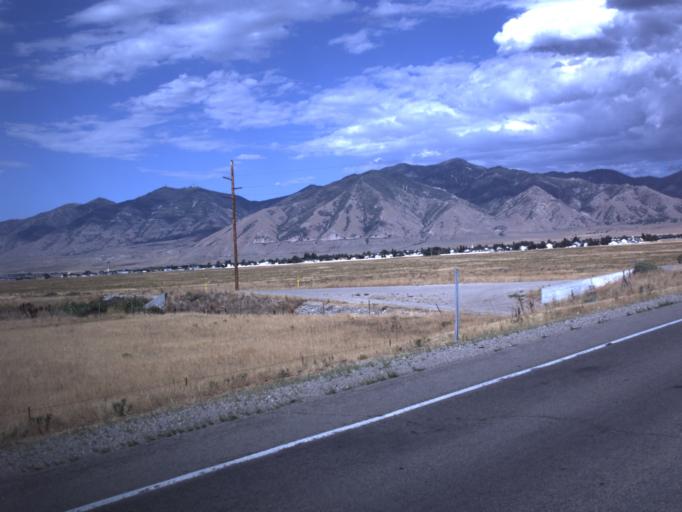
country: US
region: Utah
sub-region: Tooele County
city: Tooele
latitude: 40.5507
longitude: -112.3280
